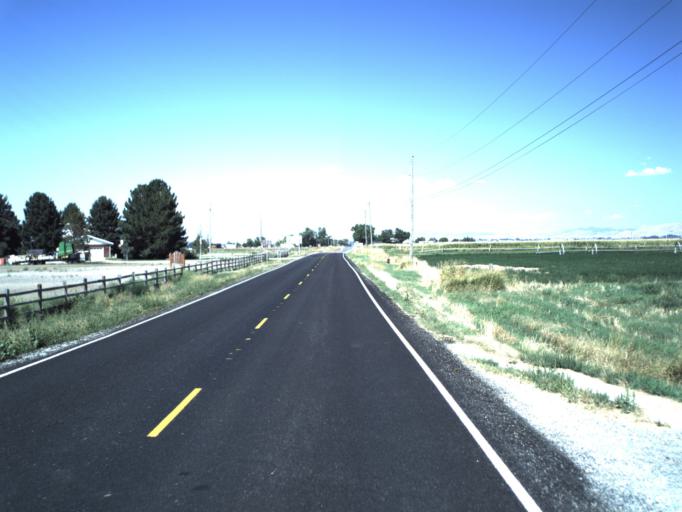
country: US
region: Utah
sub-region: Cache County
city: Lewiston
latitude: 41.9964
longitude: -111.8765
